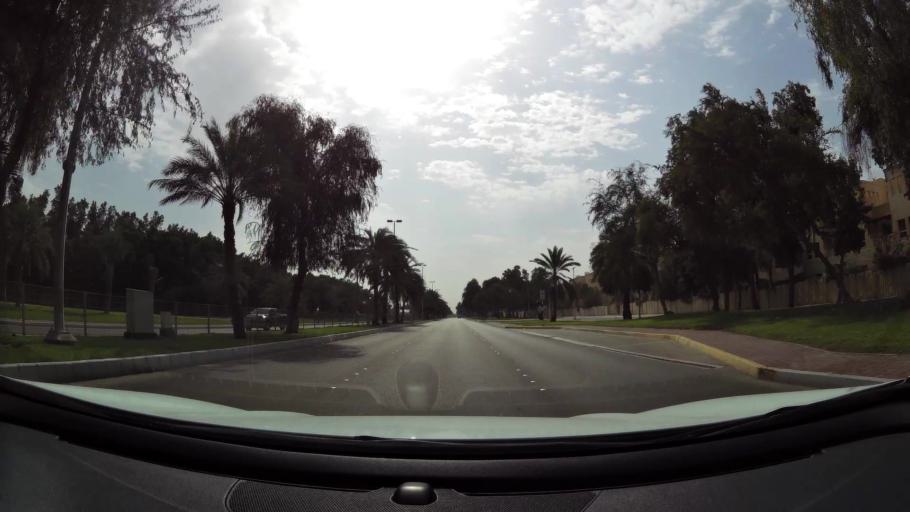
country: AE
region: Abu Dhabi
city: Abu Dhabi
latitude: 24.4455
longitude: 54.3713
